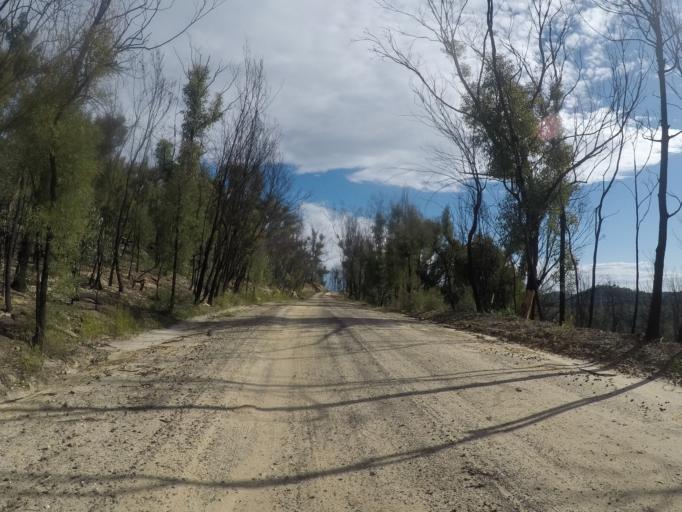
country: AU
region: New South Wales
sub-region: Hornsby Shire
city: Glenorie
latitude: -33.3626
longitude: 151.0630
